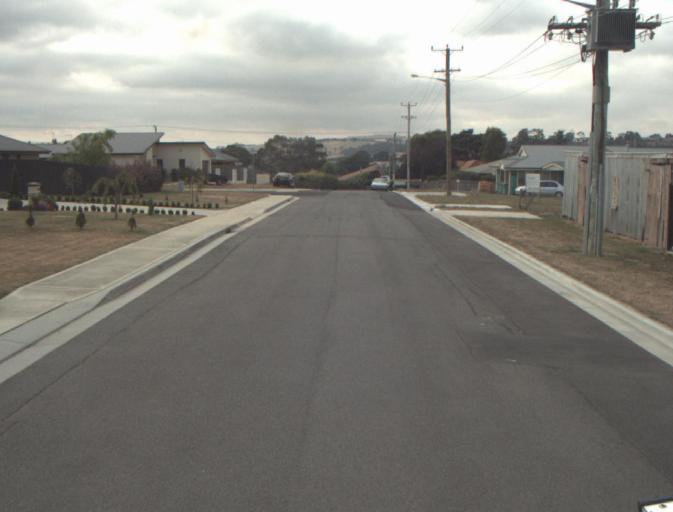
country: AU
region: Tasmania
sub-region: Launceston
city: Summerhill
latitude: -41.4818
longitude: 147.1612
